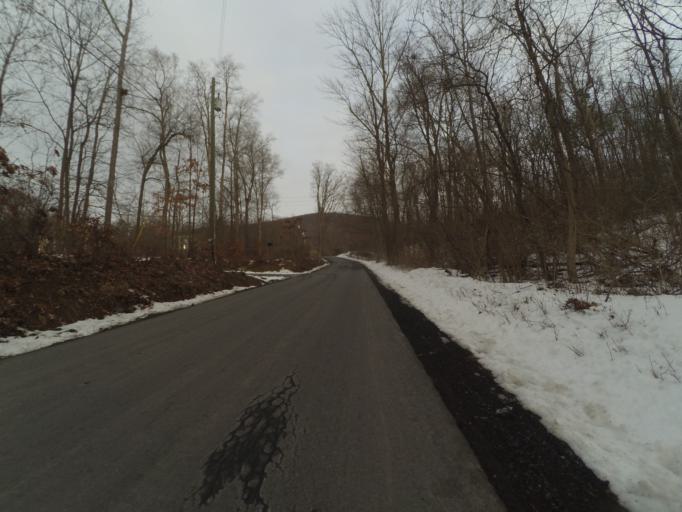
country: US
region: Pennsylvania
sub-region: Centre County
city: Lemont
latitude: 40.8097
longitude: -77.8129
